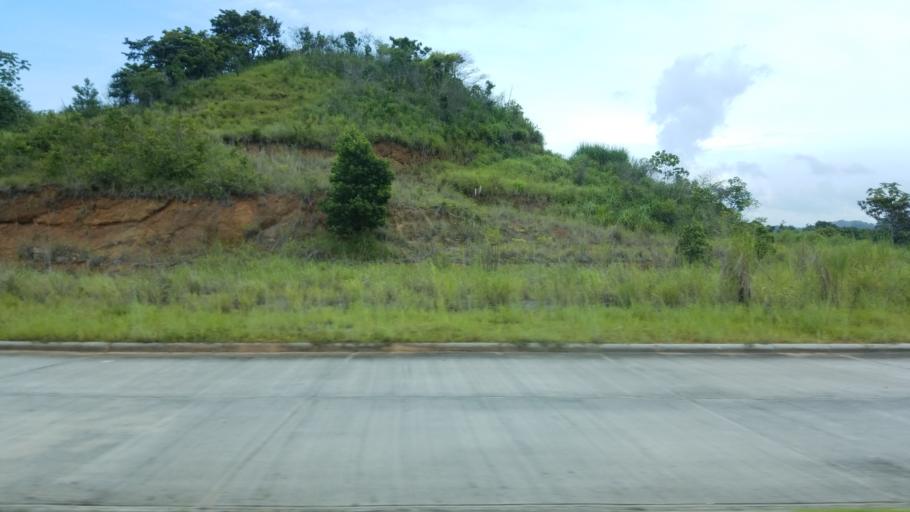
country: PA
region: Panama
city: Las Cumbres
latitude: 9.1080
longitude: -79.4751
